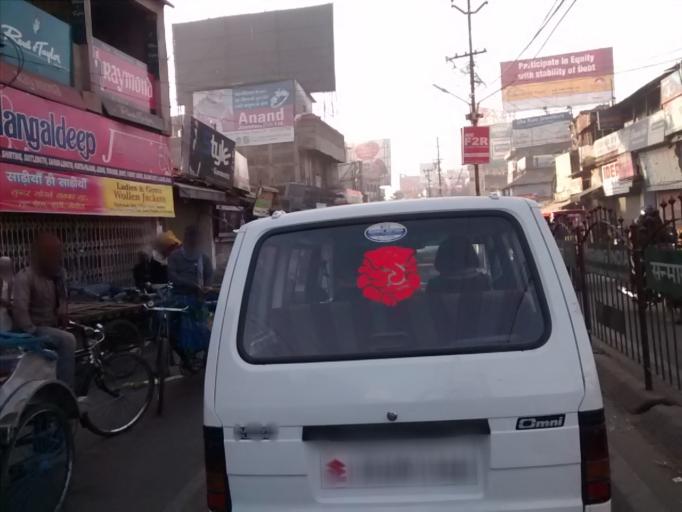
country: IN
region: Jharkhand
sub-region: Ranchi
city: Ranchi
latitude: 23.3651
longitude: 85.3251
